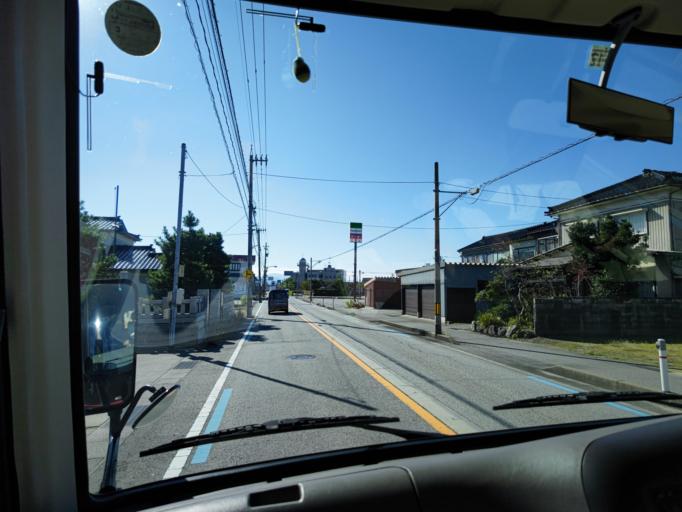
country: JP
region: Toyama
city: Nyuzen
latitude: 36.8943
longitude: 137.4194
